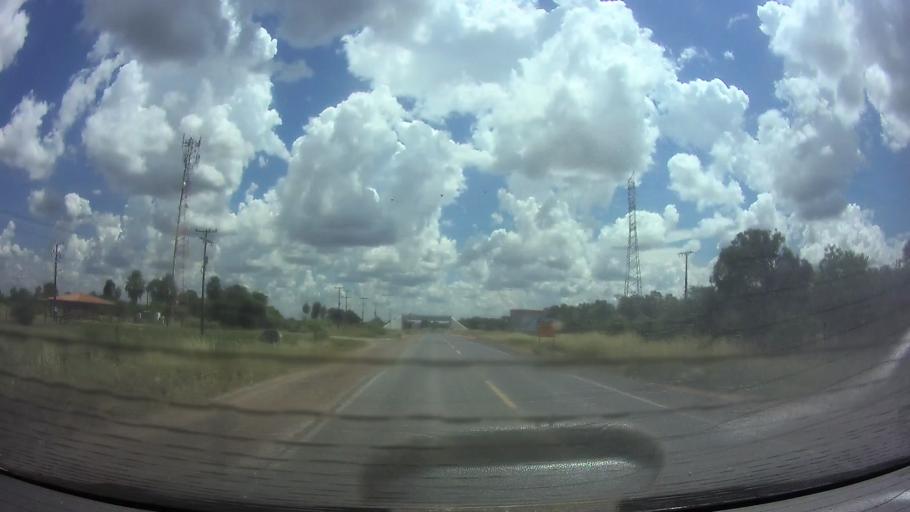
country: PY
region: Central
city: Colonia Mariano Roque Alonso
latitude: -25.1899
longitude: -57.6166
